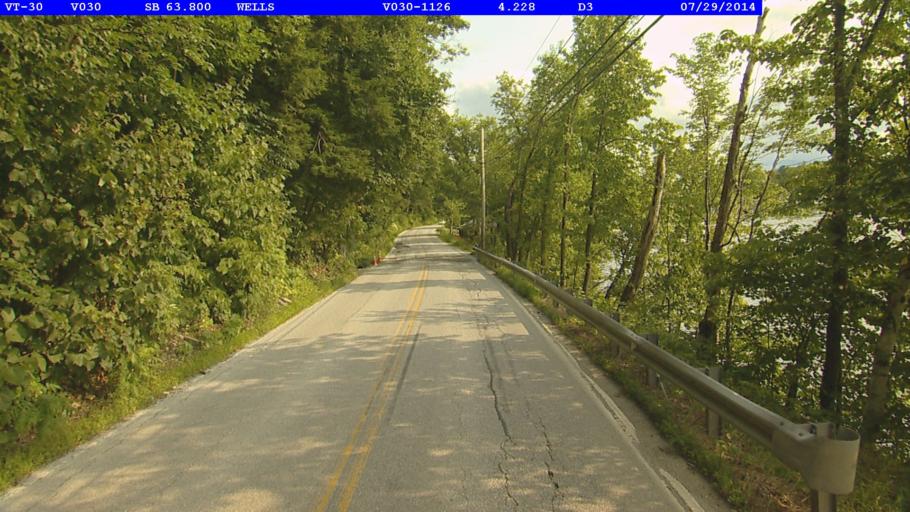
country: US
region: New York
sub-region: Washington County
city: Granville
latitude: 43.4518
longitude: -73.2040
